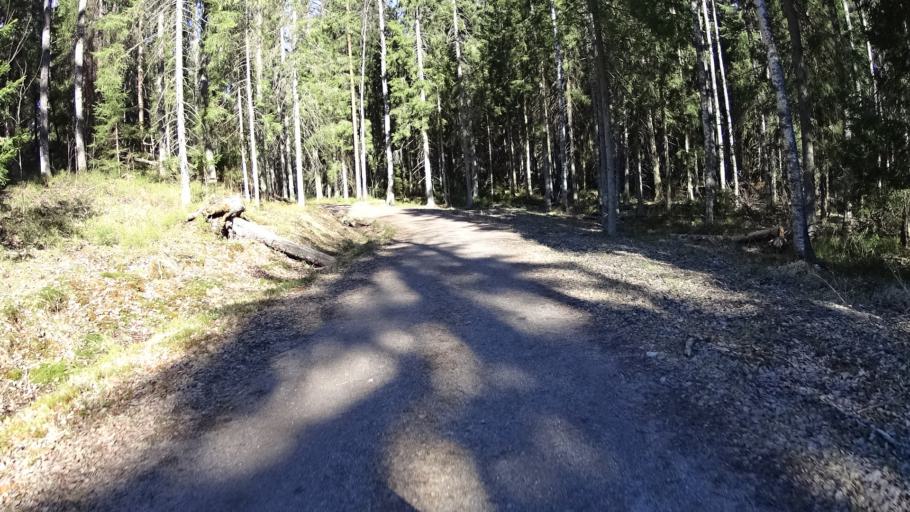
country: FI
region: Uusimaa
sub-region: Helsinki
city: Espoo
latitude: 60.2346
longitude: 24.6381
